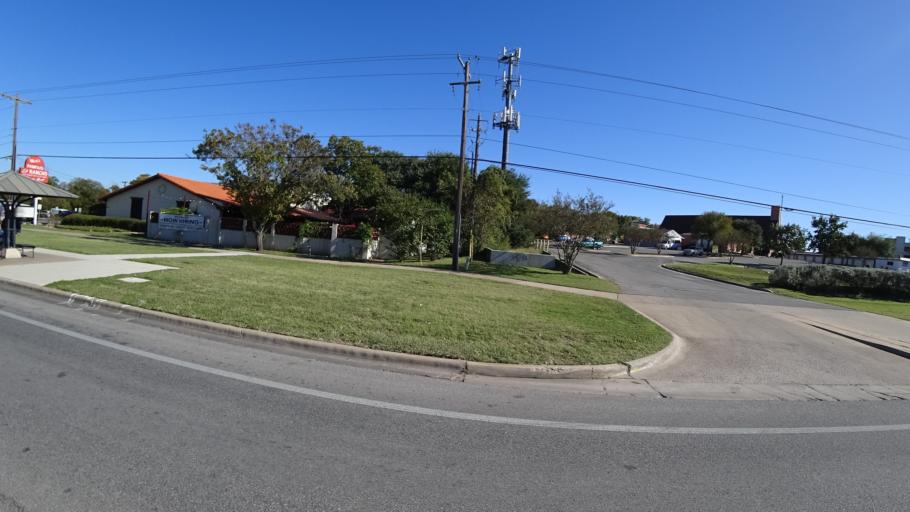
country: US
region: Texas
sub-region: Travis County
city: Rollingwood
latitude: 30.2454
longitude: -97.7798
